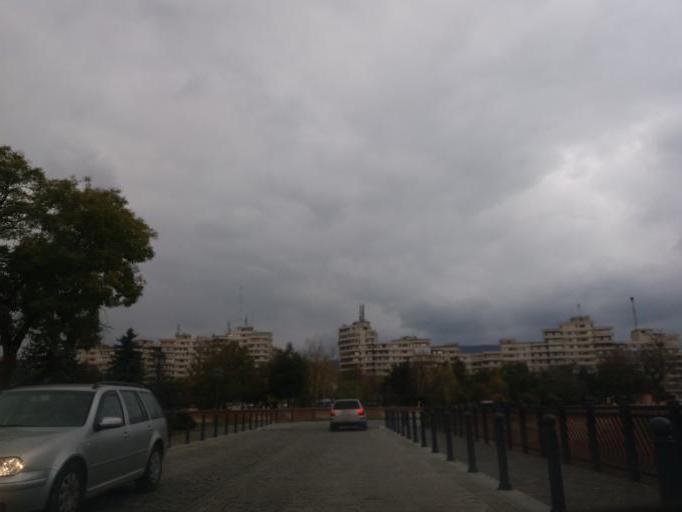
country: RO
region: Alba
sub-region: Municipiul Alba Iulia
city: Alba Iulia
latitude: 46.0691
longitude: 23.5675
